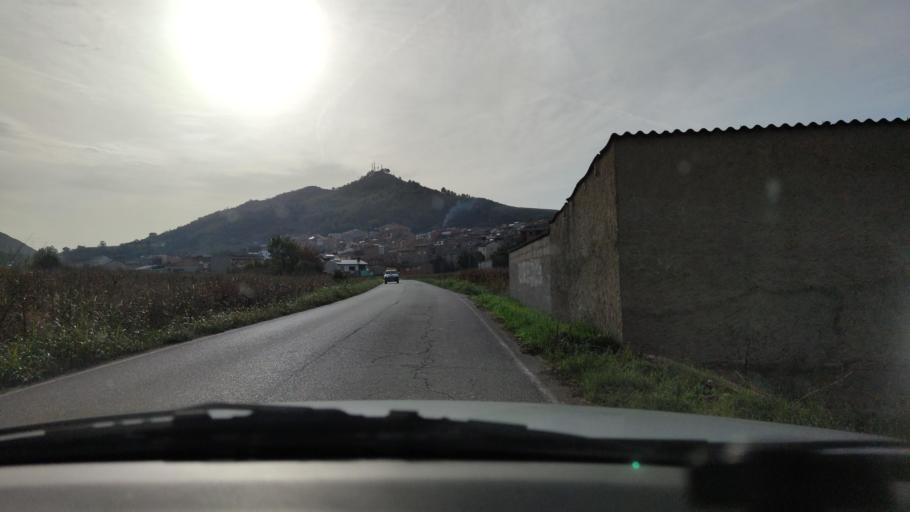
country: ES
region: Catalonia
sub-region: Provincia de Lleida
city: Artesa de Segre
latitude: 41.8992
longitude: 1.0471
